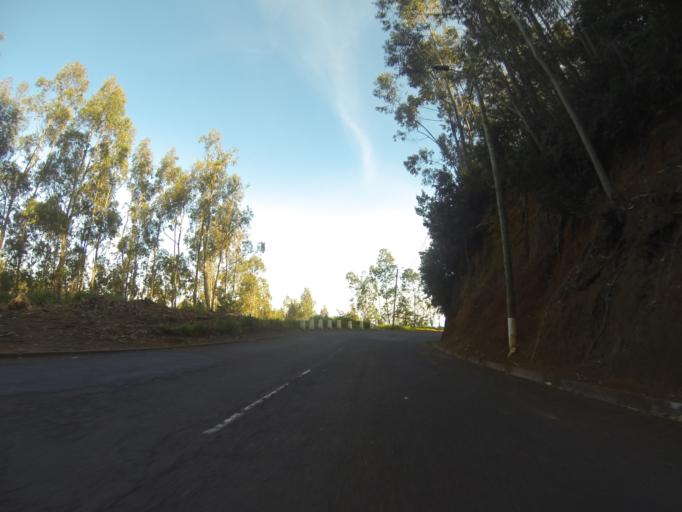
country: PT
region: Madeira
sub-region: Santa Cruz
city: Camacha
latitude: 32.6707
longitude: -16.8677
